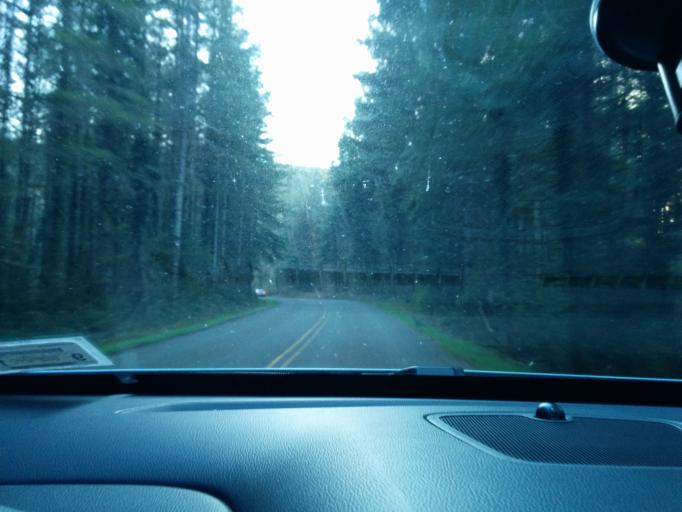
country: US
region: Washington
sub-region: Snohomish County
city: Sultan
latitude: 47.8996
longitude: -121.7606
